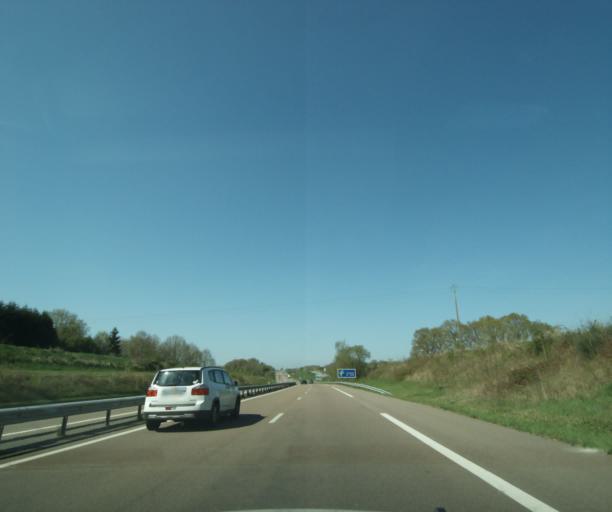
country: FR
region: Bourgogne
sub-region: Departement de la Nievre
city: Cosne-Cours-sur-Loire
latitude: 47.4191
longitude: 2.9455
